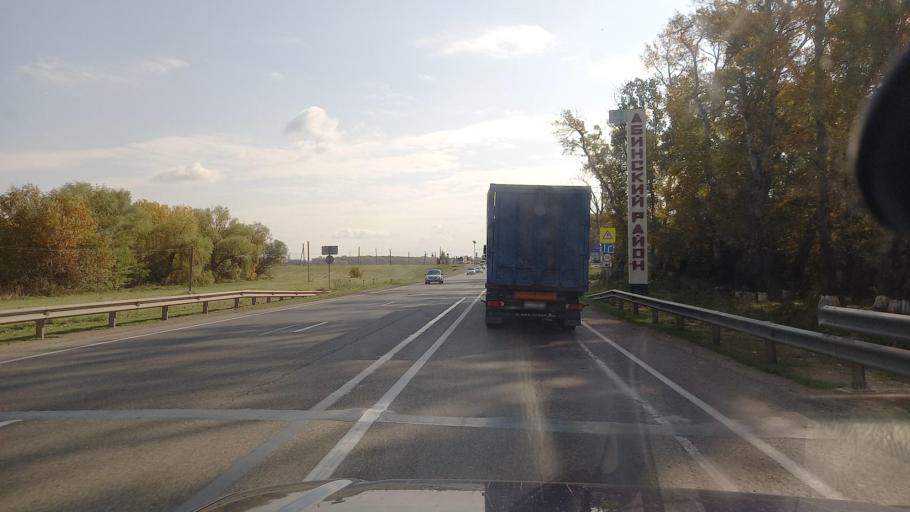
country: RU
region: Krasnodarskiy
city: Novoukrainskiy
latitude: 44.8854
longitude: 38.0857
